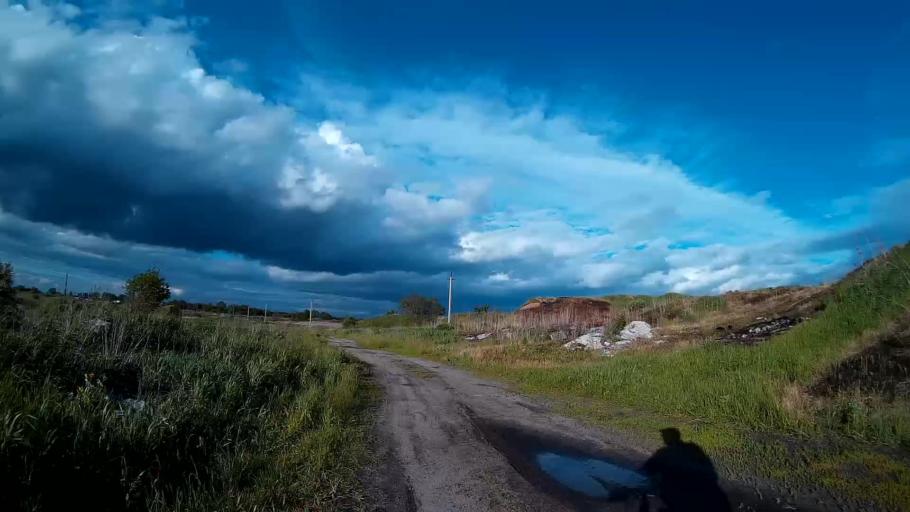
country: RU
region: Ulyanovsk
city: Novoul'yanovsk
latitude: 54.2079
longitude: 48.2717
